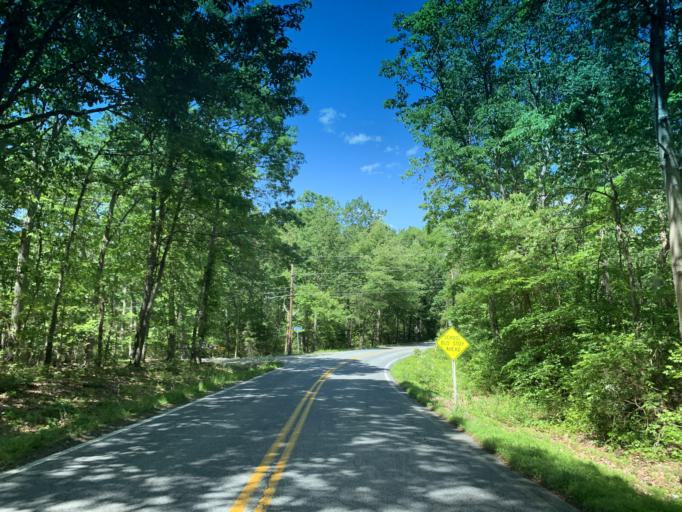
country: US
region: Maryland
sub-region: Cecil County
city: North East
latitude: 39.5550
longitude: -75.8993
